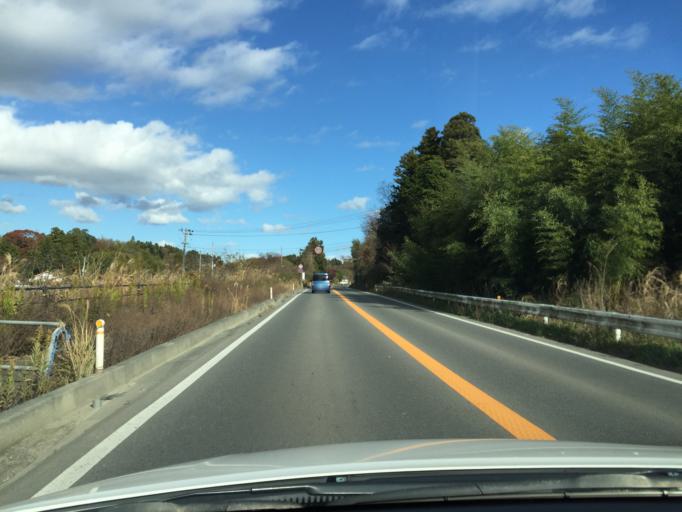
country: JP
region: Fukushima
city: Namie
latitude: 37.5680
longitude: 141.0037
